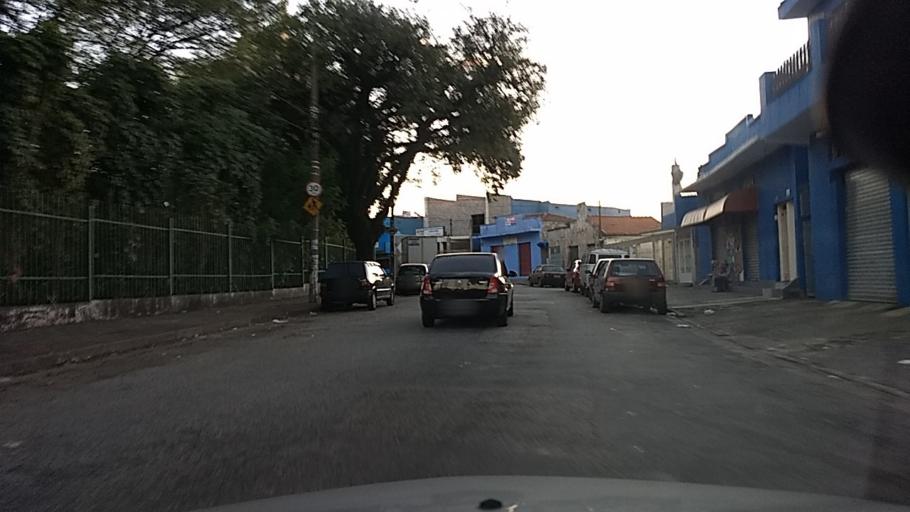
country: BR
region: Sao Paulo
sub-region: Sao Paulo
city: Sao Paulo
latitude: -23.5035
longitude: -46.5920
